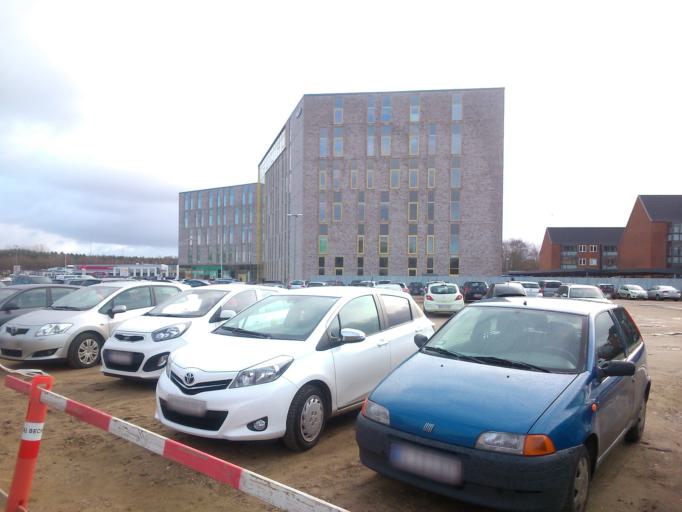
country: DK
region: Central Jutland
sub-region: Holstebro Kommune
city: Holstebro
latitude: 56.3706
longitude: 8.6228
